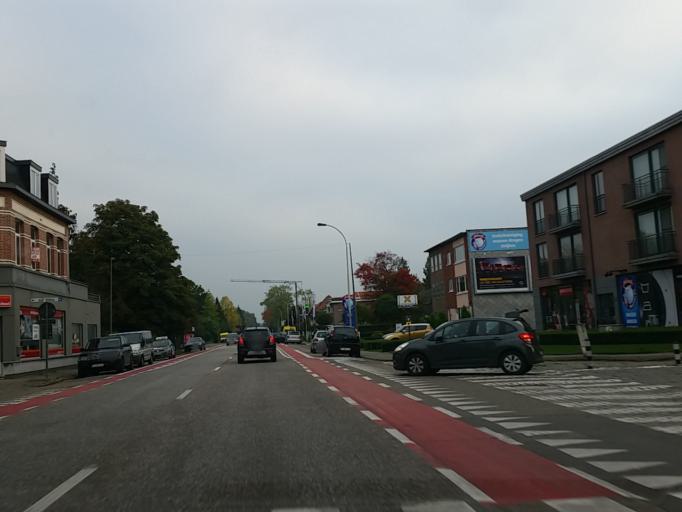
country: BE
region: Flanders
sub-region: Provincie Antwerpen
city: Kapellen
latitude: 51.2902
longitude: 4.4456
